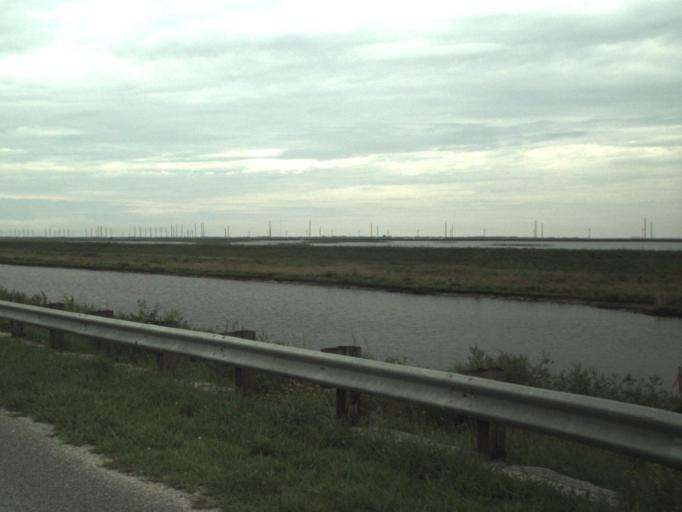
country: US
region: Florida
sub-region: Palm Beach County
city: Loxahatchee Groves
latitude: 26.6850
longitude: -80.3634
